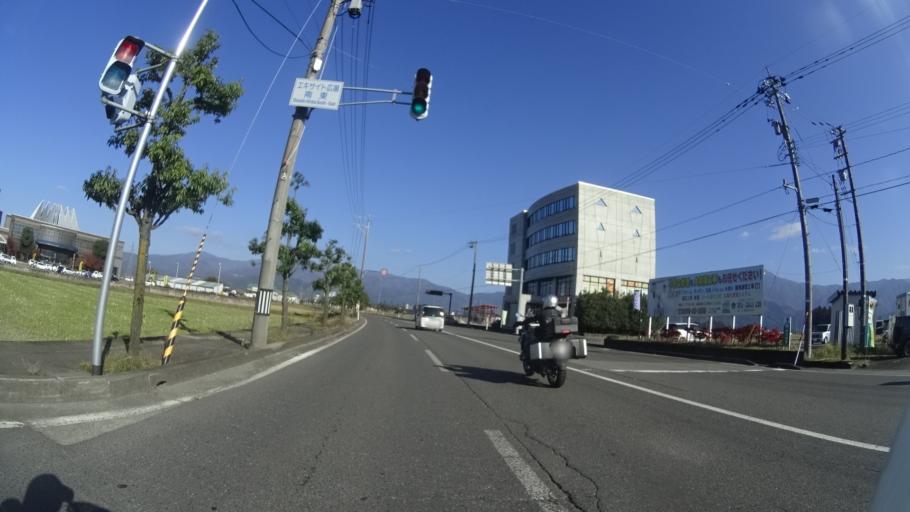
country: JP
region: Fukui
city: Ono
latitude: 35.9705
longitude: 136.5047
